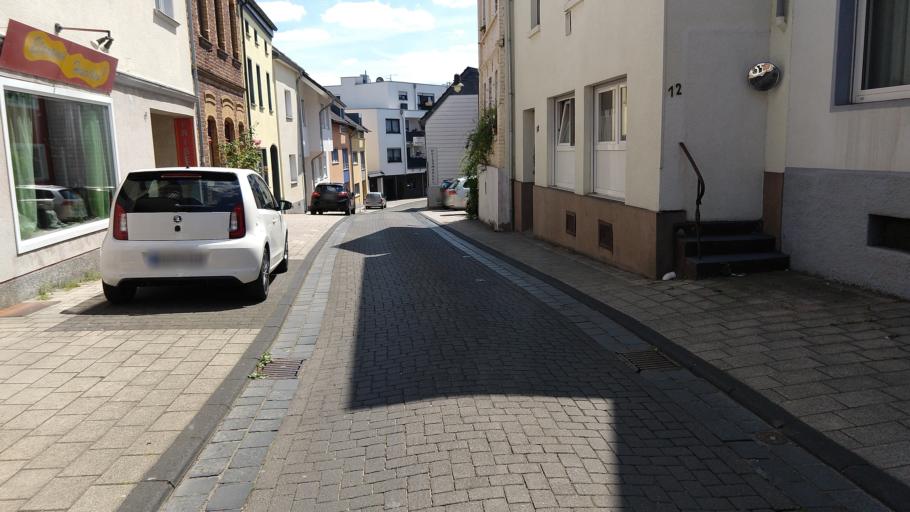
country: DE
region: North Rhine-Westphalia
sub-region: Regierungsbezirk Koln
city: Alfter
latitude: 50.7374
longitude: 7.0080
